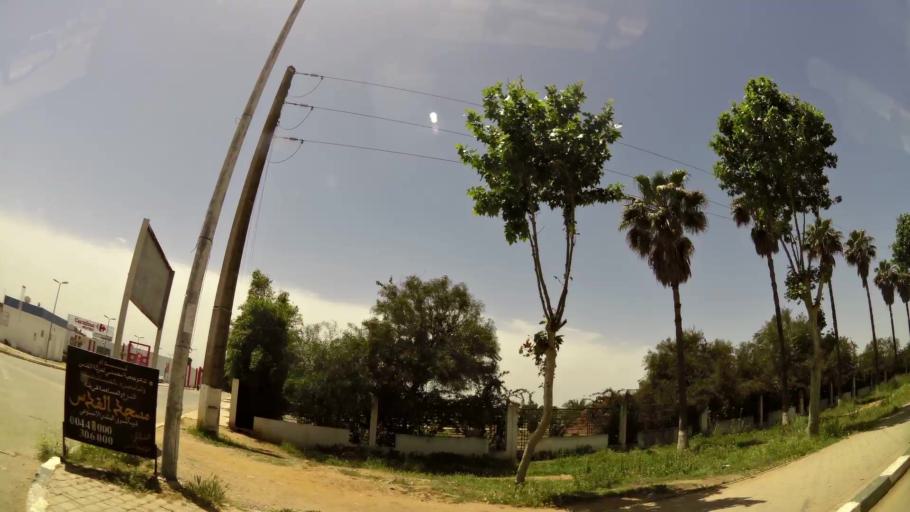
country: MA
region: Rabat-Sale-Zemmour-Zaer
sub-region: Khemisset
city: Khemisset
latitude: 33.8276
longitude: -6.0913
